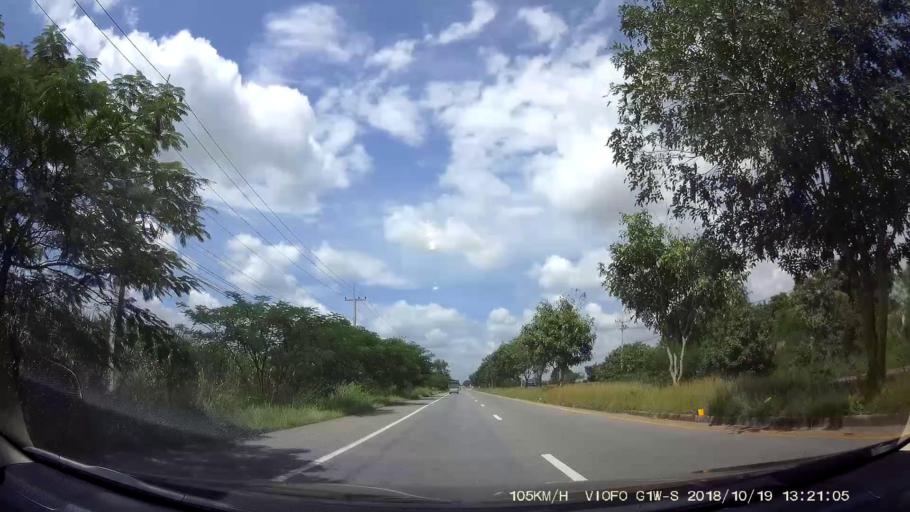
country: TH
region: Chaiyaphum
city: Chatturat
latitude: 15.4560
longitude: 101.8269
